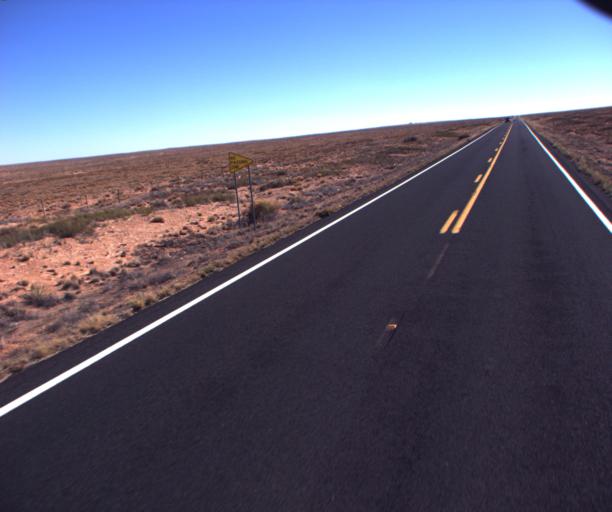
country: US
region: Arizona
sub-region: Coconino County
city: Tuba City
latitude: 36.0181
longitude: -111.1081
